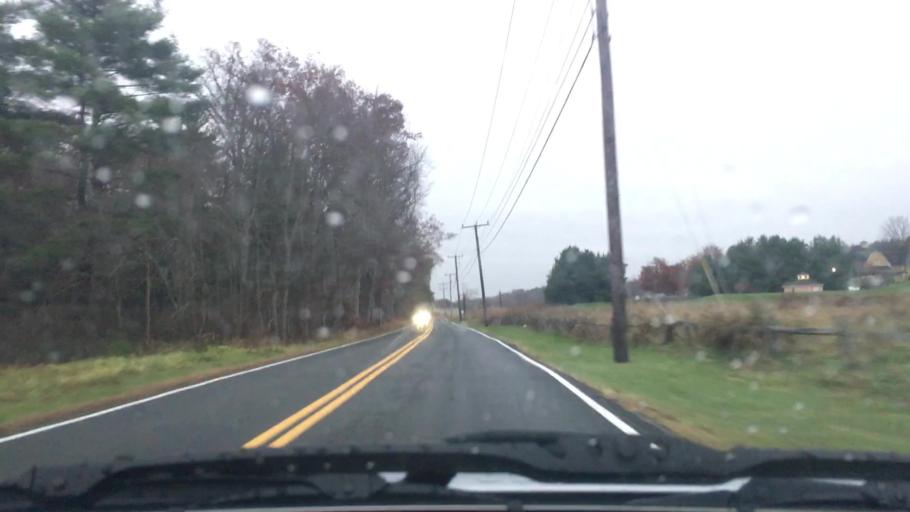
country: US
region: Massachusetts
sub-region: Hampden County
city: Southwick
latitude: 42.0876
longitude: -72.7753
